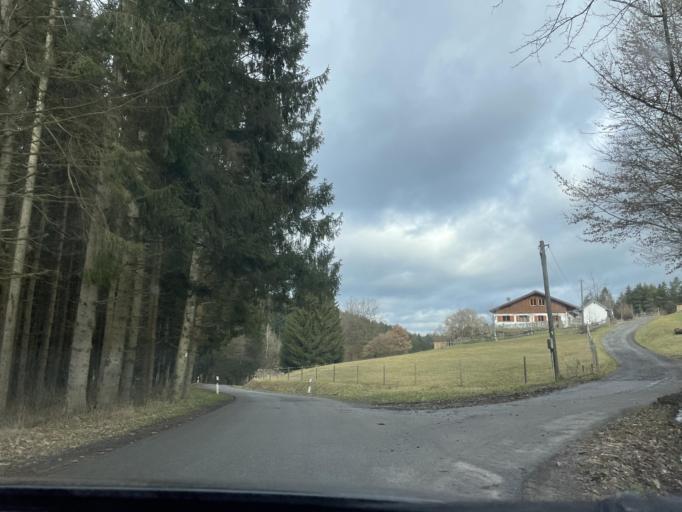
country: DE
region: Bavaria
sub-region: Lower Bavaria
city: Prackenbach
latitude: 49.1199
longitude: 12.8412
